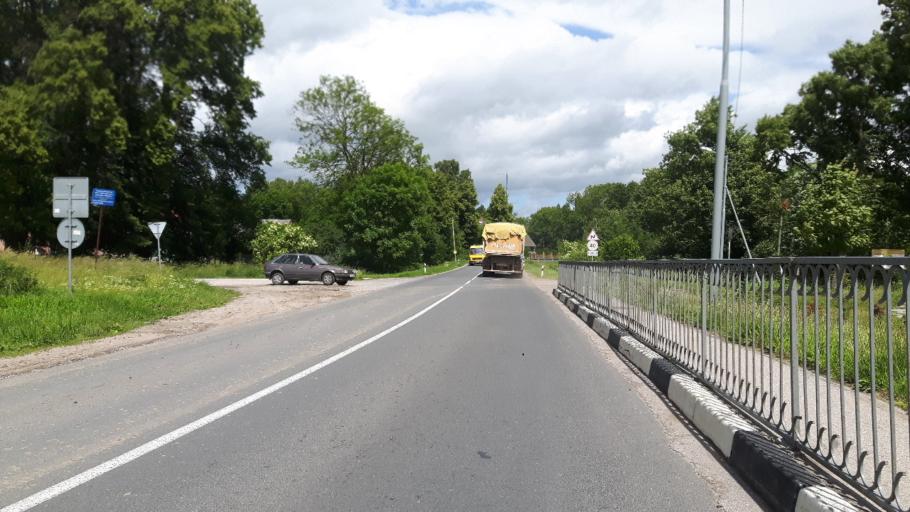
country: RU
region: Kaliningrad
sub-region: Gorod Kaliningrad
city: Kaliningrad
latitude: 54.8164
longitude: 20.4178
